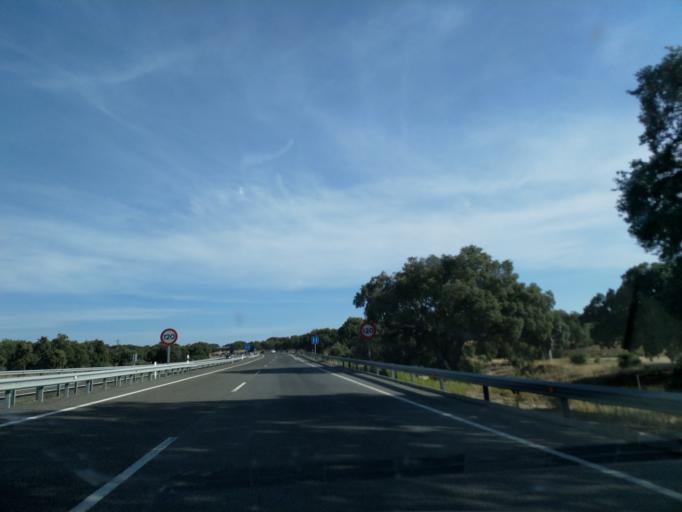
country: ES
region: Castille and Leon
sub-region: Provincia de Avila
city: Avila
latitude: 40.6746
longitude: -4.6809
